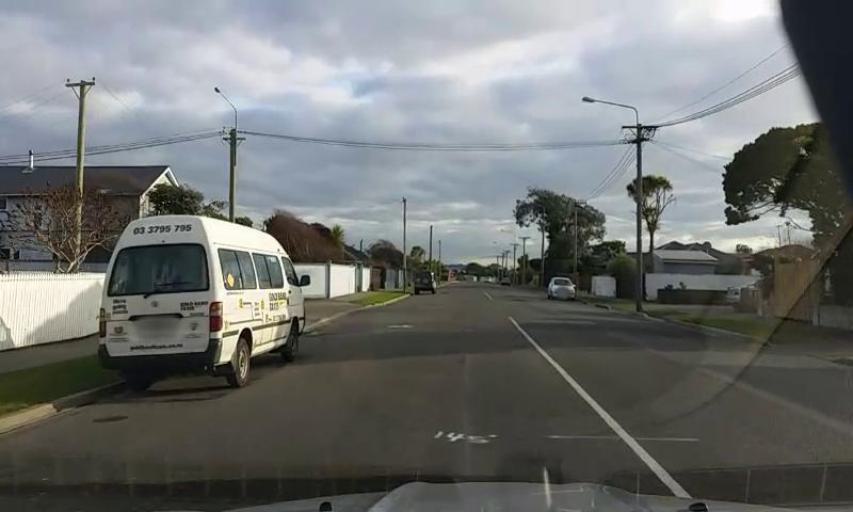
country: NZ
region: Canterbury
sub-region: Christchurch City
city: Christchurch
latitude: -43.5211
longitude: 172.7317
